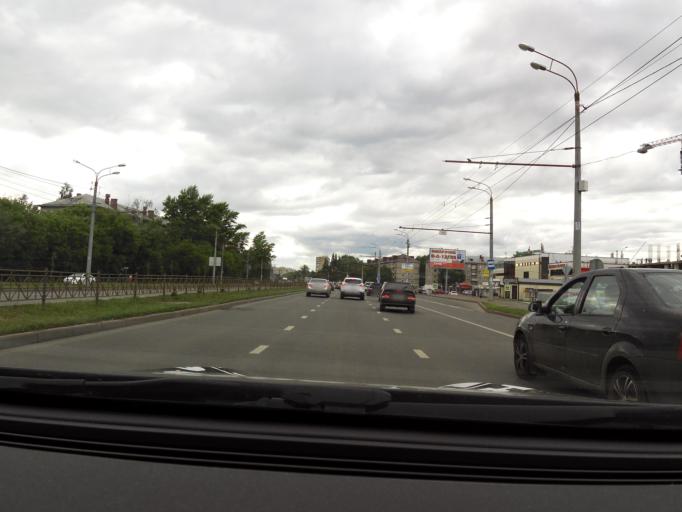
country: RU
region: Tatarstan
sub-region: Gorod Kazan'
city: Kazan
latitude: 55.8163
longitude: 49.0658
